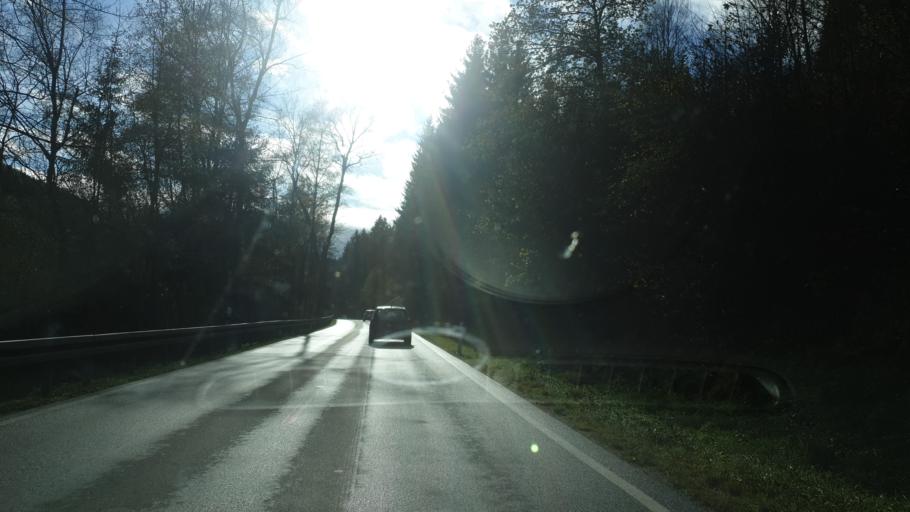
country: DE
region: Saxony
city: Zschorlau
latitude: 50.5353
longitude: 12.6519
